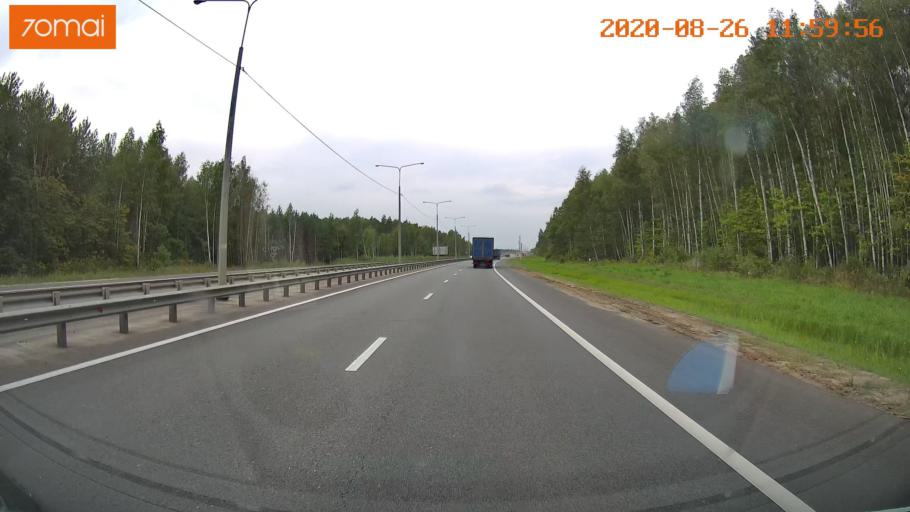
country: RU
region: Rjazan
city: Kiritsy
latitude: 54.2862
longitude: 40.2863
